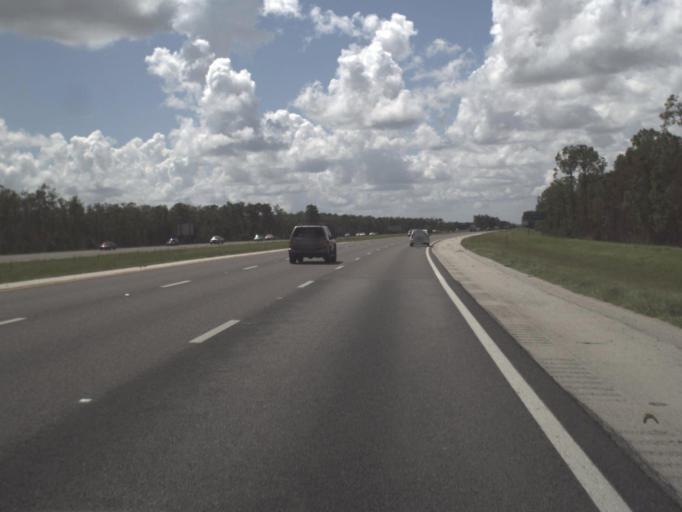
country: US
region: Florida
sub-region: Lee County
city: Estero
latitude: 26.4203
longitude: -81.7739
